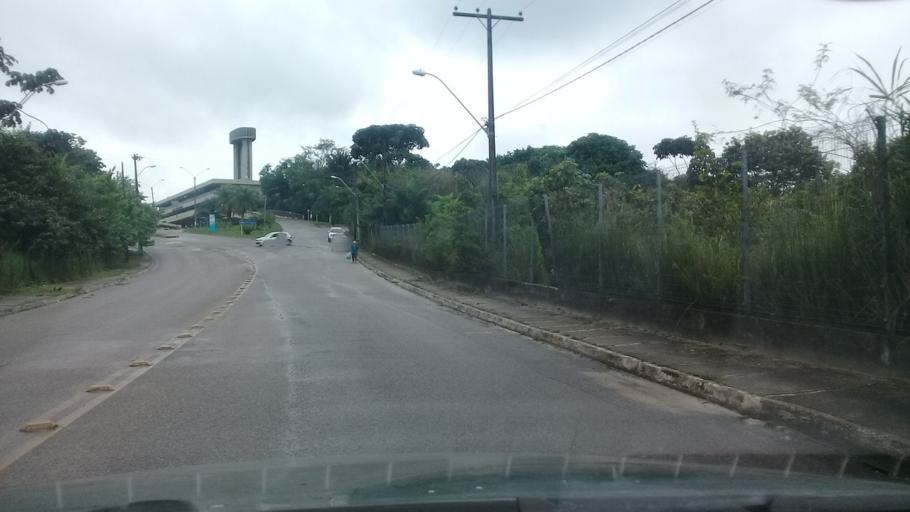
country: BR
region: Pernambuco
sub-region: Jaboatao Dos Guararapes
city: Jaboatao dos Guararapes
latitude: -8.0636
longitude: -34.9850
